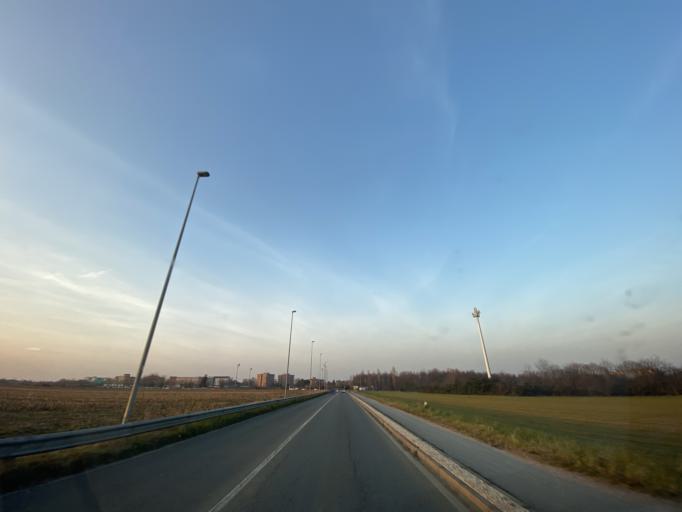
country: IT
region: Lombardy
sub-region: Citta metropolitana di Milano
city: Solaro
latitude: 45.6080
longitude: 9.0796
